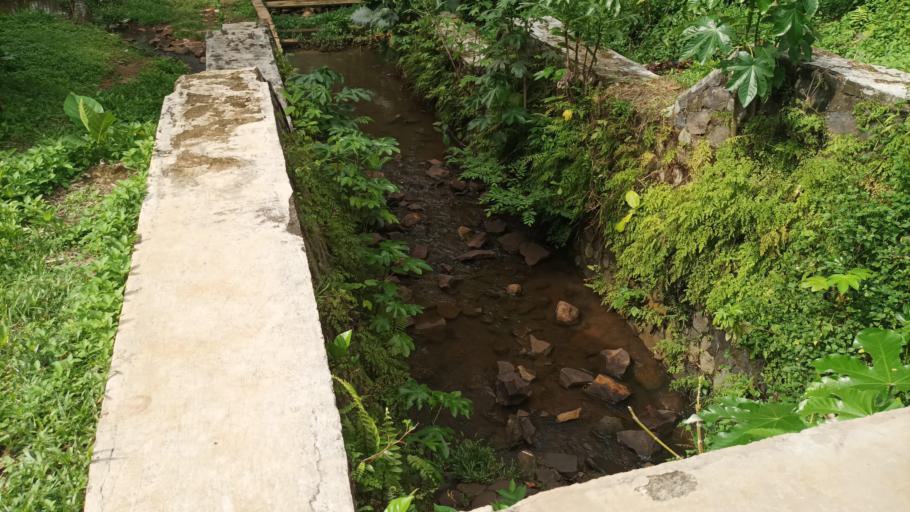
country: ID
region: West Java
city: Depok
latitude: -6.4325
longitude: 106.8429
